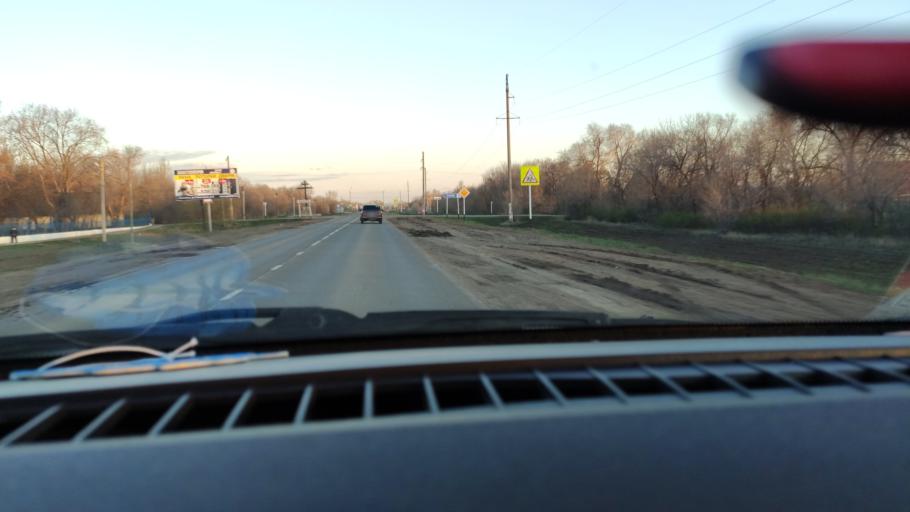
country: RU
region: Saratov
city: Privolzhskiy
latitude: 51.3859
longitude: 46.0393
